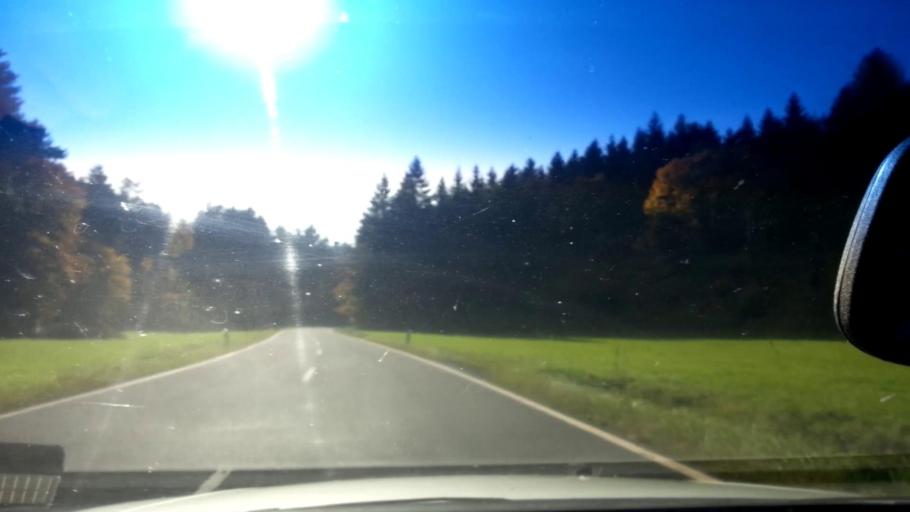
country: DE
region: Bavaria
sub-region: Upper Franconia
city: Poxdorf
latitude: 49.9817
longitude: 11.1293
